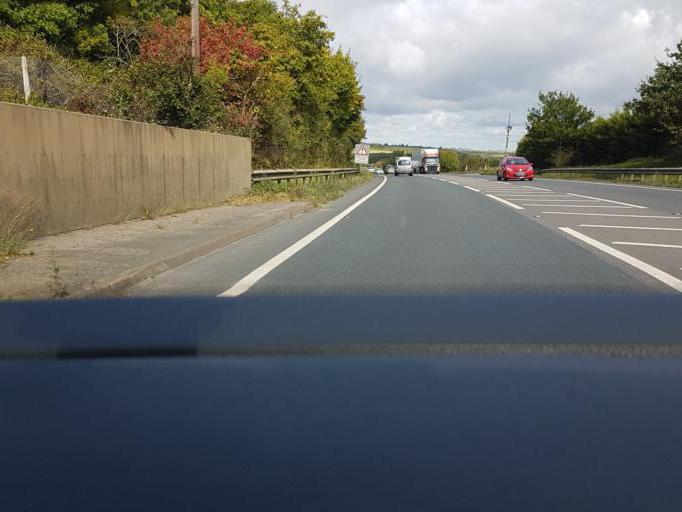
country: GB
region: England
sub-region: Worcestershire
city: Badsey
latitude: 52.1000
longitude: -1.9228
